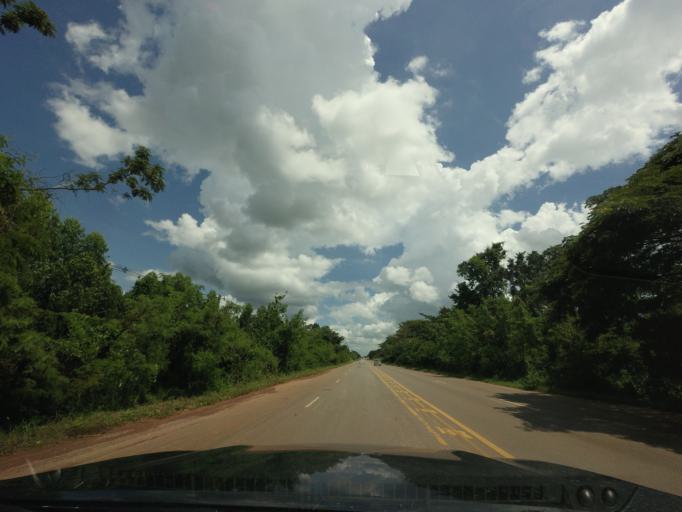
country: TH
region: Changwat Udon Thani
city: Ban Dung
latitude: 17.6811
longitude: 103.2284
